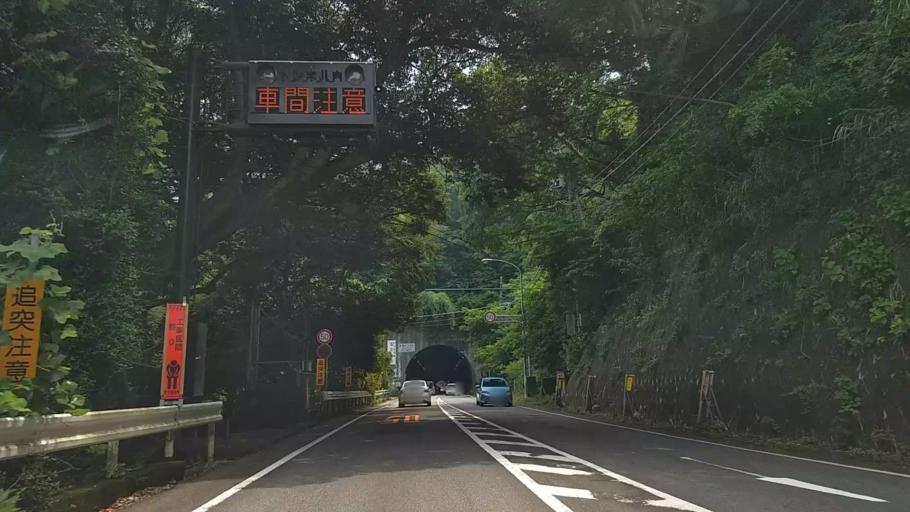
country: JP
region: Shizuoka
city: Atami
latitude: 35.0739
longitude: 139.0758
